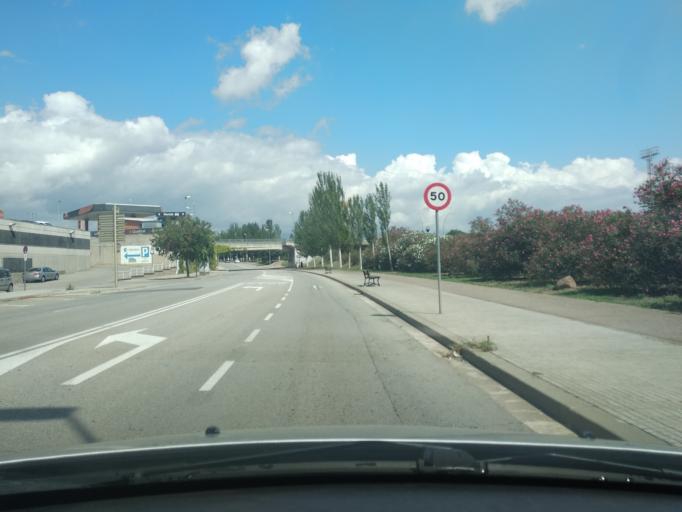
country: ES
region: Catalonia
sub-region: Provincia de Barcelona
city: Granollers
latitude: 41.6005
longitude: 2.2782
